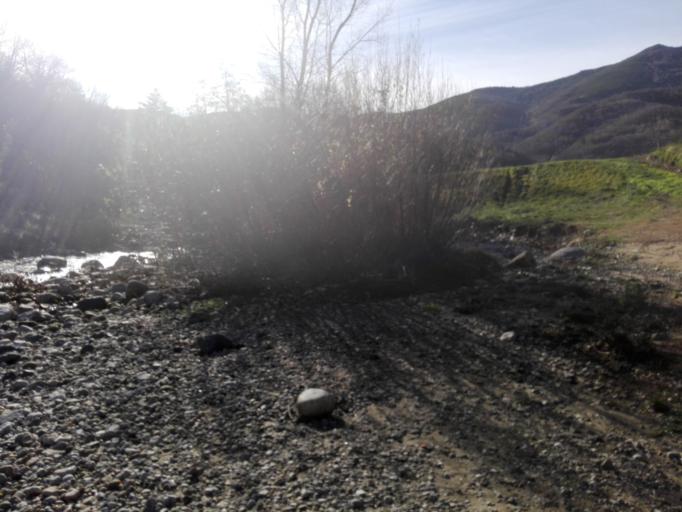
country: FR
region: Rhone-Alpes
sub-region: Departement de l'Ardeche
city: Thueyts
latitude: 44.7425
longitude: 4.2465
